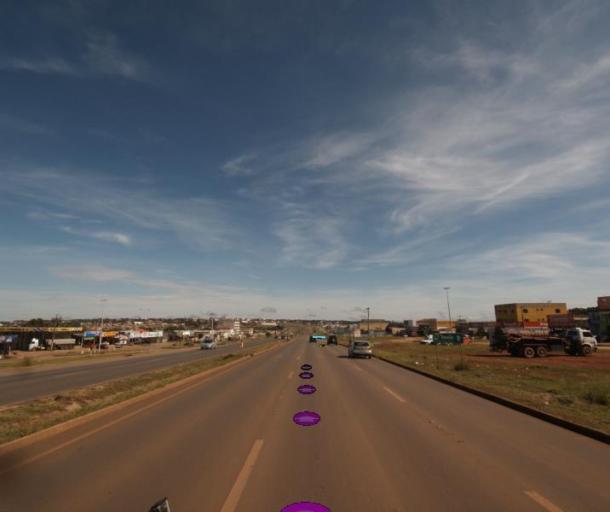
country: BR
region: Federal District
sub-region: Brasilia
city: Brasilia
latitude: -15.7469
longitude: -48.2648
